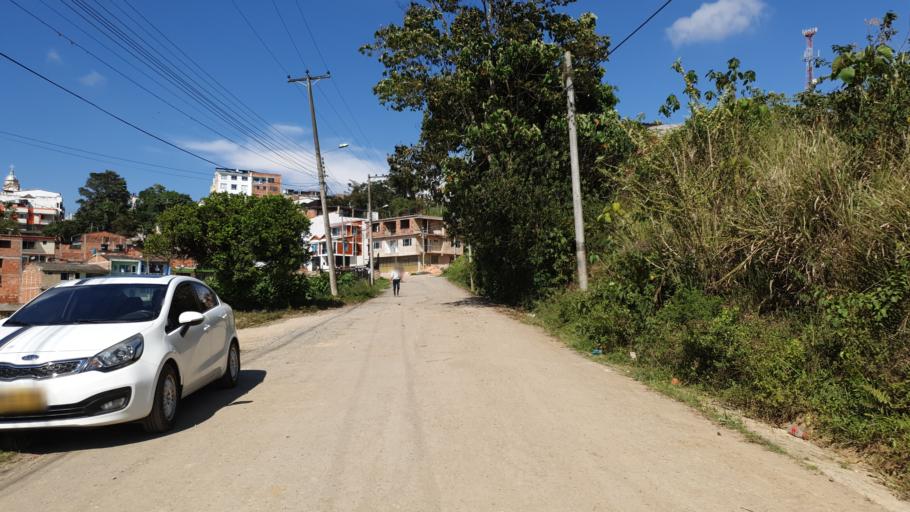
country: CO
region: Boyaca
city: Santana
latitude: 6.0554
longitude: -73.4841
